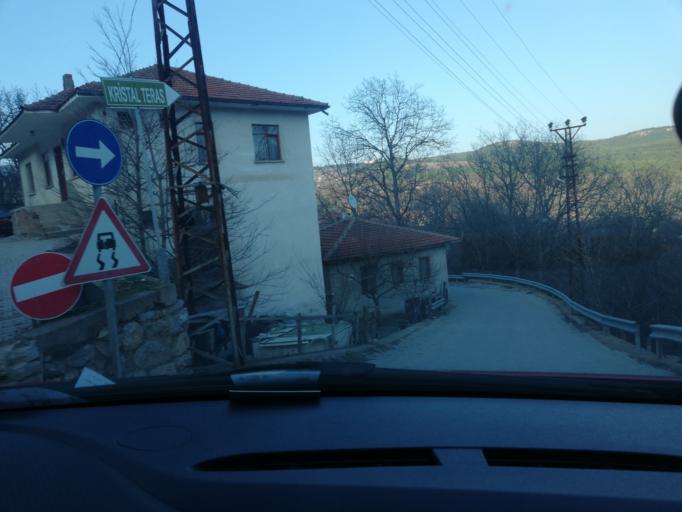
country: TR
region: Karabuk
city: Safranbolu
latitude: 41.2821
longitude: 32.6761
